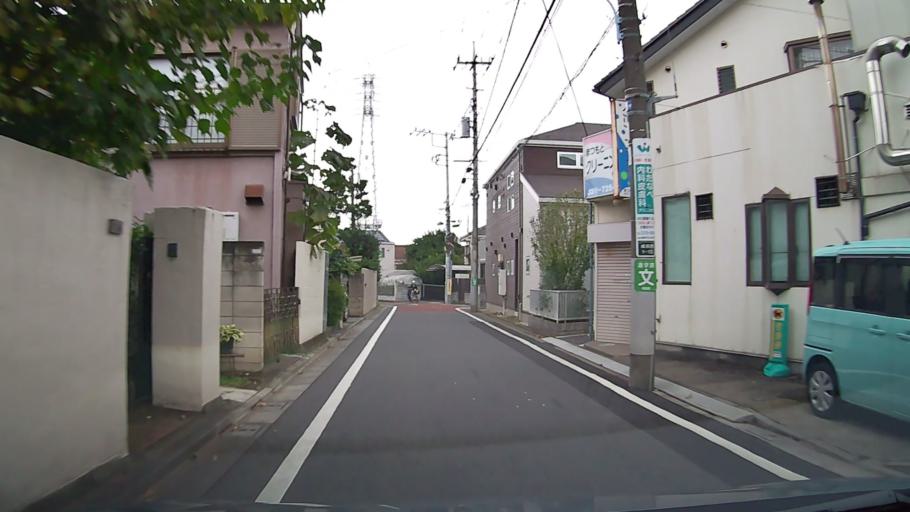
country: JP
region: Tokyo
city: Tokyo
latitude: 35.6871
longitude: 139.6302
